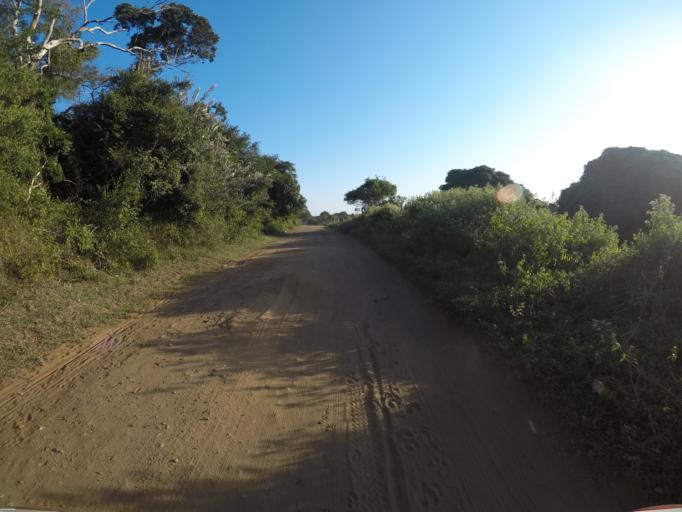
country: ZA
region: KwaZulu-Natal
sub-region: uThungulu District Municipality
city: KwaMbonambi
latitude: -28.7047
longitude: 32.1880
